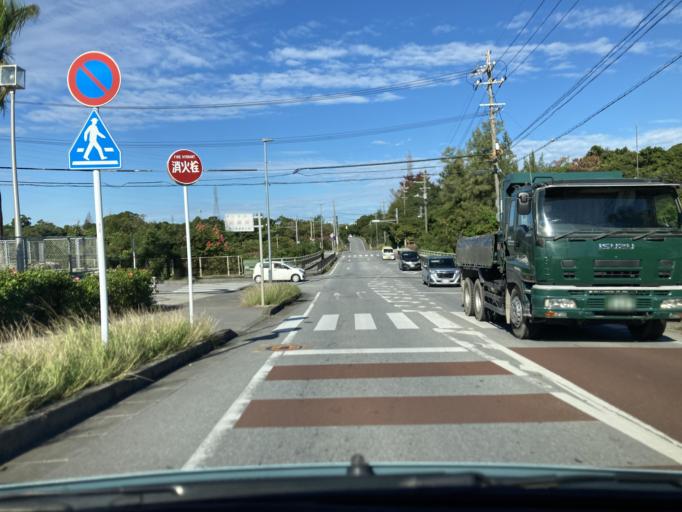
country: JP
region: Okinawa
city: Okinawa
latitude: 26.3700
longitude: 127.7705
